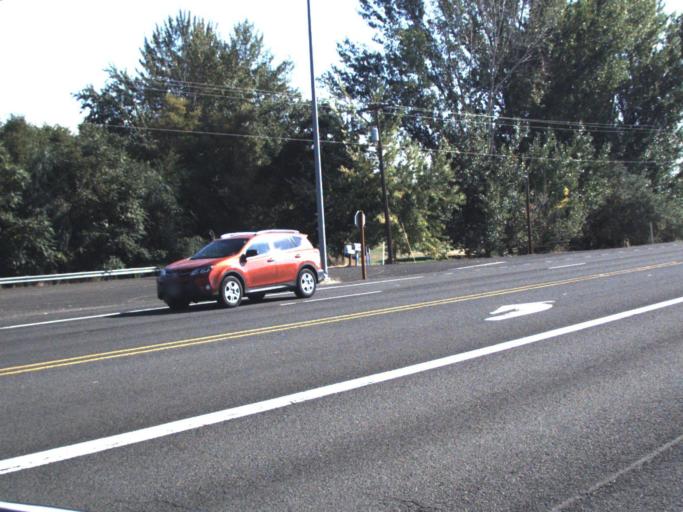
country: US
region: Washington
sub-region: Walla Walla County
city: College Place
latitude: 46.0118
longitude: -118.3896
